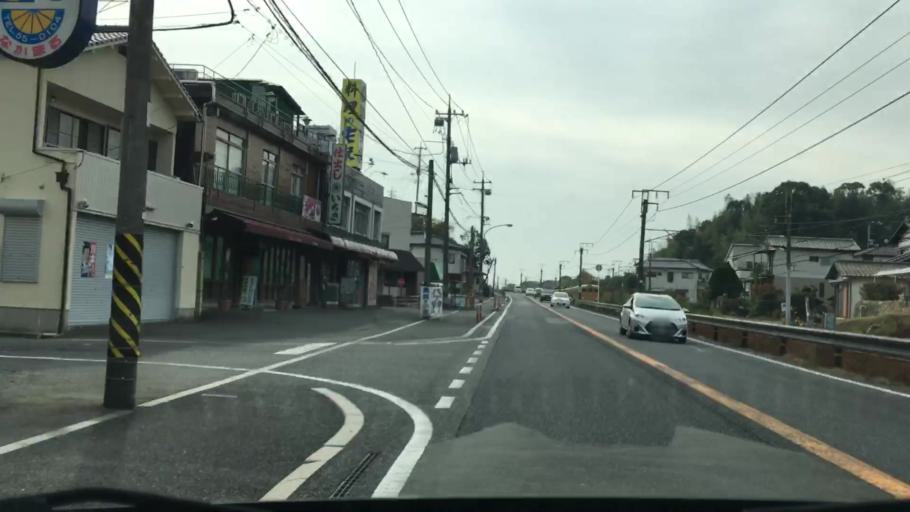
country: JP
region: Hiroshima
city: Ono-hara
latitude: 34.2789
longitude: 132.2627
